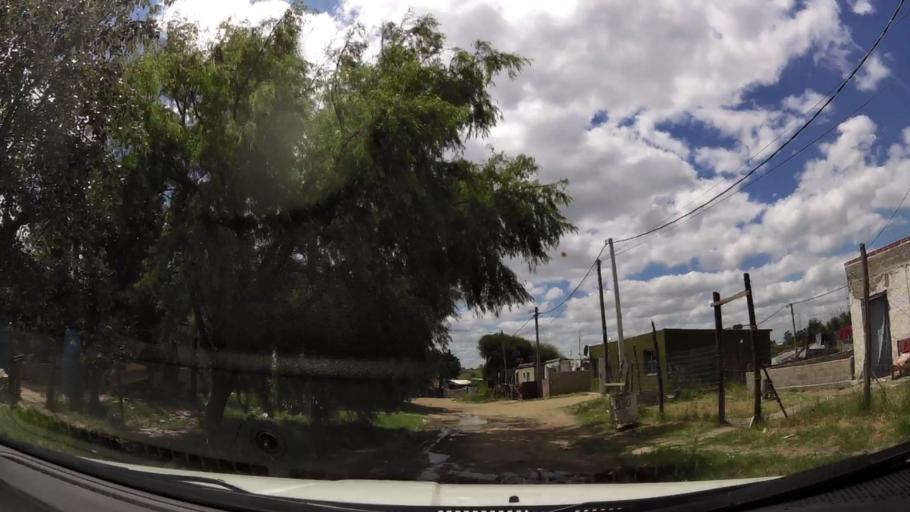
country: UY
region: Canelones
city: La Paz
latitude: -34.8189
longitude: -56.2480
